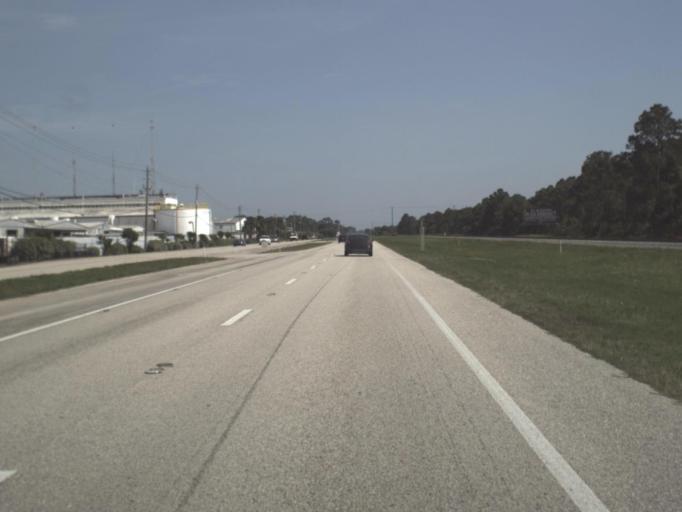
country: US
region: Florida
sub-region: Saint Johns County
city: Villano Beach
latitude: 29.9588
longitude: -81.3464
